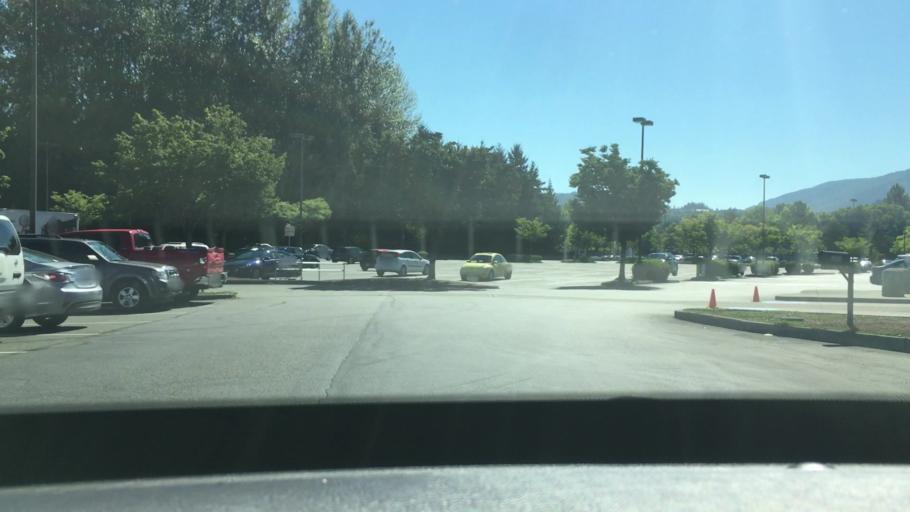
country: US
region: Washington
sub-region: King County
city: Issaquah
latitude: 47.5480
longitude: -122.0563
